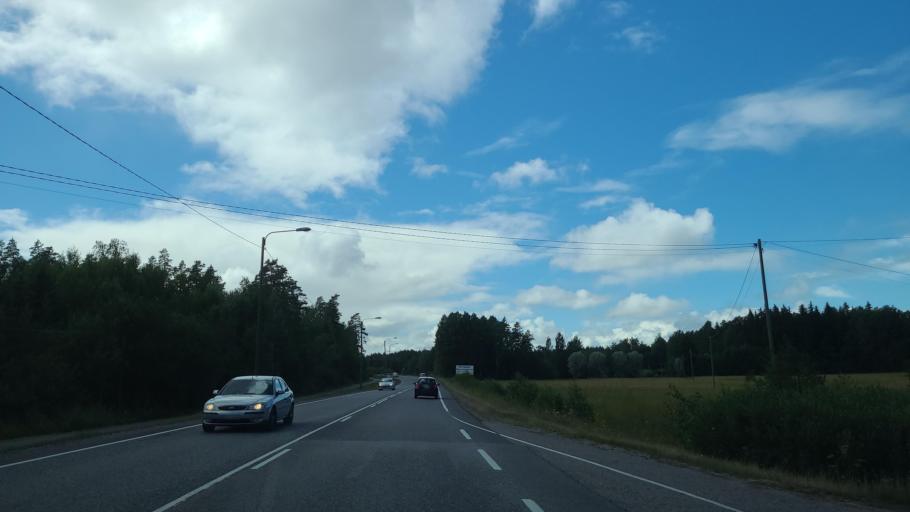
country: FI
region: Varsinais-Suomi
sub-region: Aboland-Turunmaa
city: Pargas
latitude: 60.3315
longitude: 22.3575
